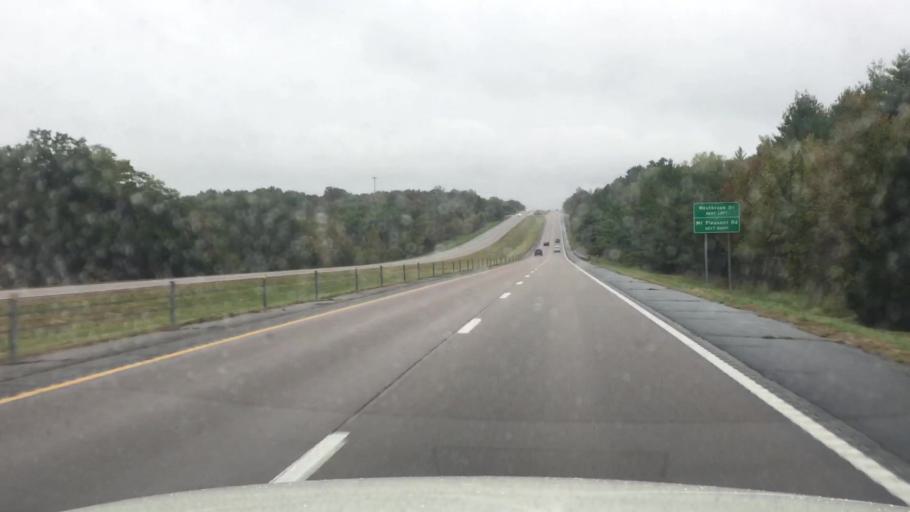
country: US
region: Missouri
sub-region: Boone County
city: Ashland
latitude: 38.7044
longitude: -92.2548
